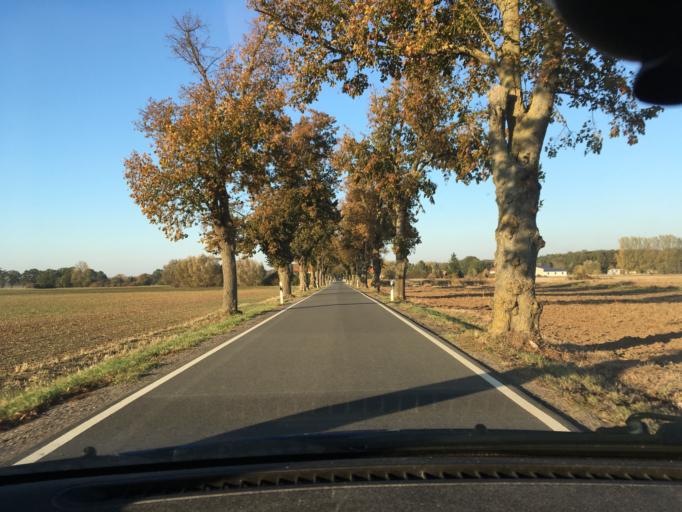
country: DE
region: Lower Saxony
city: Bleckede
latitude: 53.3250
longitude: 10.7999
